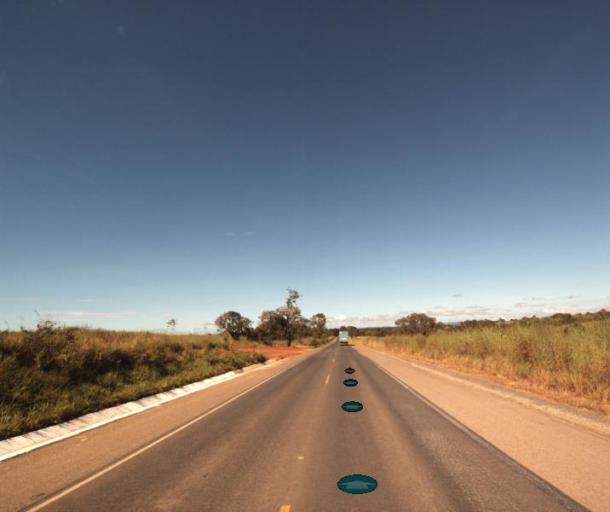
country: BR
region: Goias
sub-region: Itapaci
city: Itapaci
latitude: -14.9666
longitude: -49.3873
